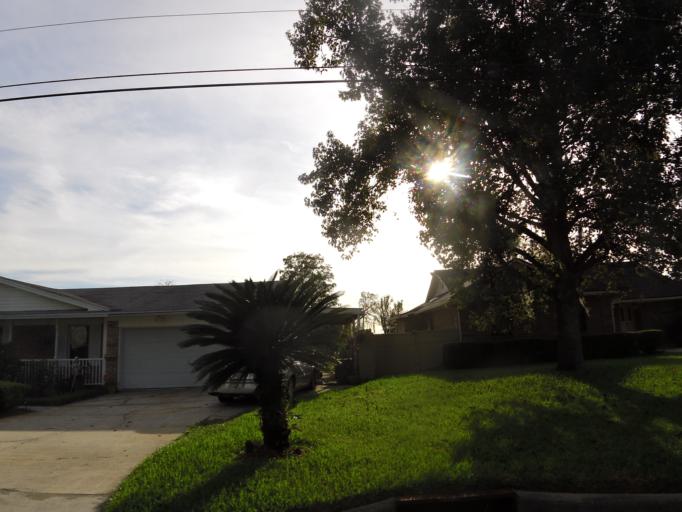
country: US
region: Florida
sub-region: Duval County
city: Jacksonville
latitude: 30.4170
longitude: -81.6675
